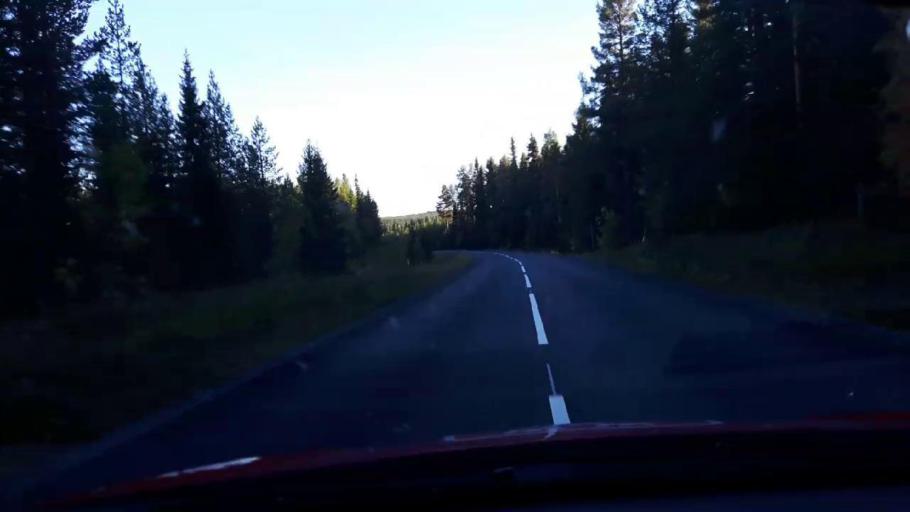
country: SE
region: Jaemtland
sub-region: OEstersunds Kommun
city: Lit
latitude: 63.5266
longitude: 14.8445
